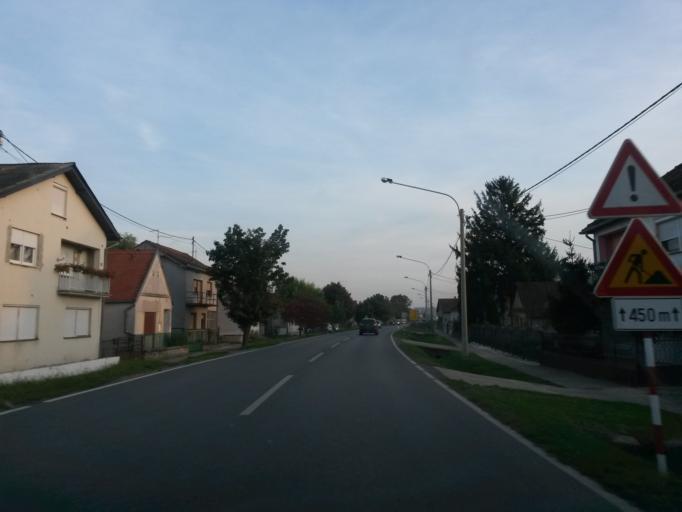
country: HR
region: Osjecko-Baranjska
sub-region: Grad Osijek
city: Bilje
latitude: 45.6078
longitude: 18.7420
